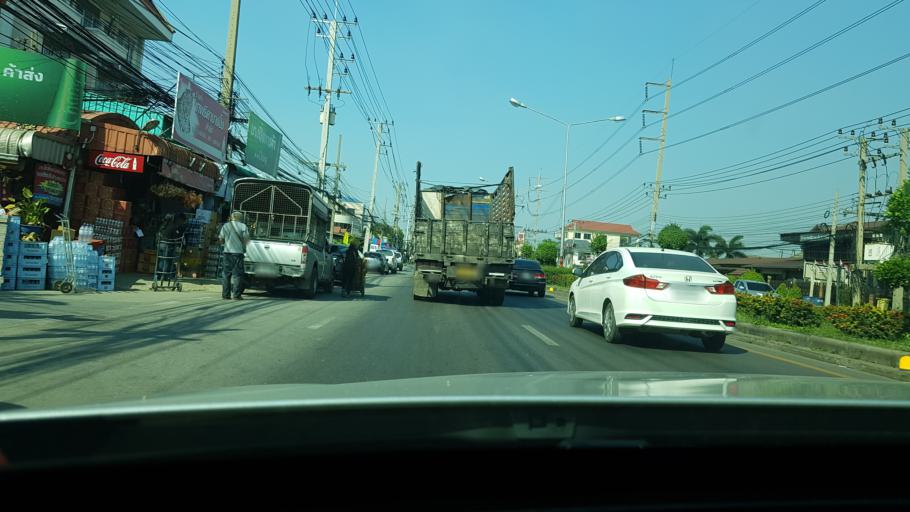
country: TH
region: Samut Sakhon
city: Samut Sakhon
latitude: 13.5971
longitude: 100.2828
